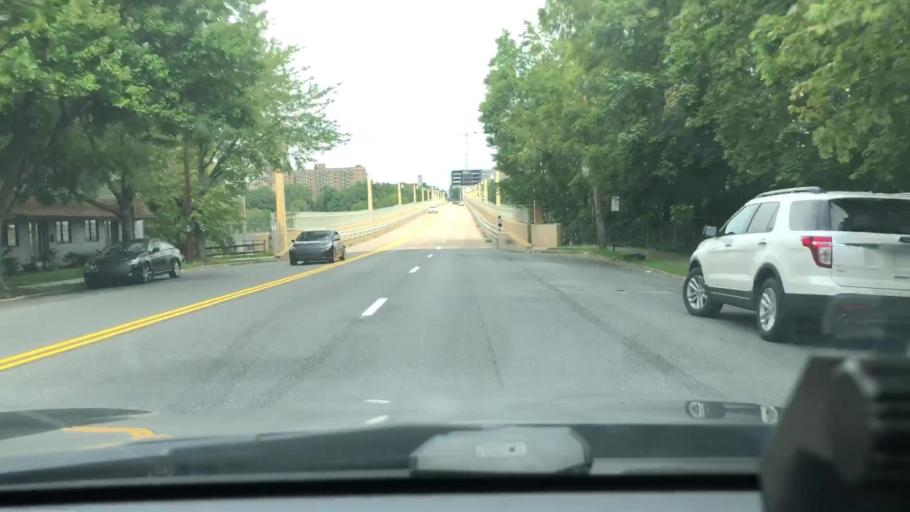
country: US
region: Pennsylvania
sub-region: Lehigh County
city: Allentown
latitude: 40.5934
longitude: -75.4698
